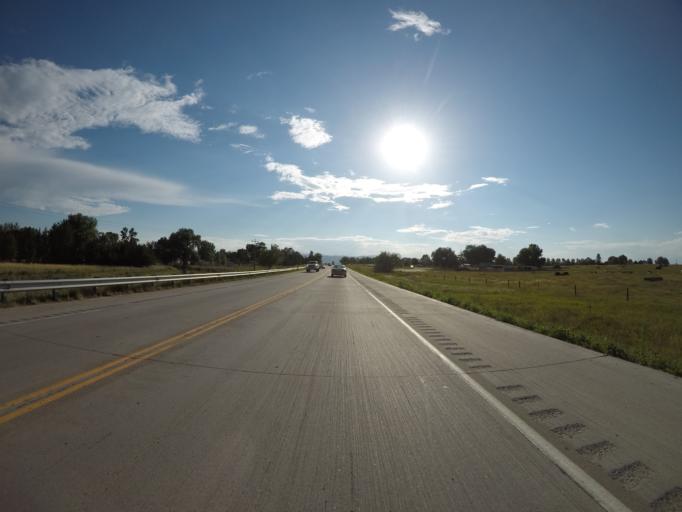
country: US
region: Colorado
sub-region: Larimer County
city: Fort Collins
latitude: 40.5813
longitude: -104.9726
